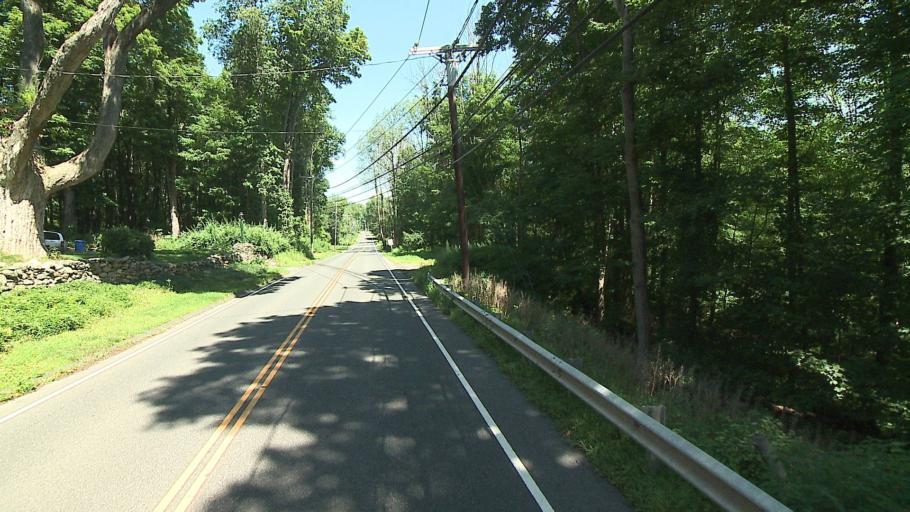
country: US
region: Connecticut
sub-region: New Haven County
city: Oxford
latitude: 41.3613
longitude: -73.1923
